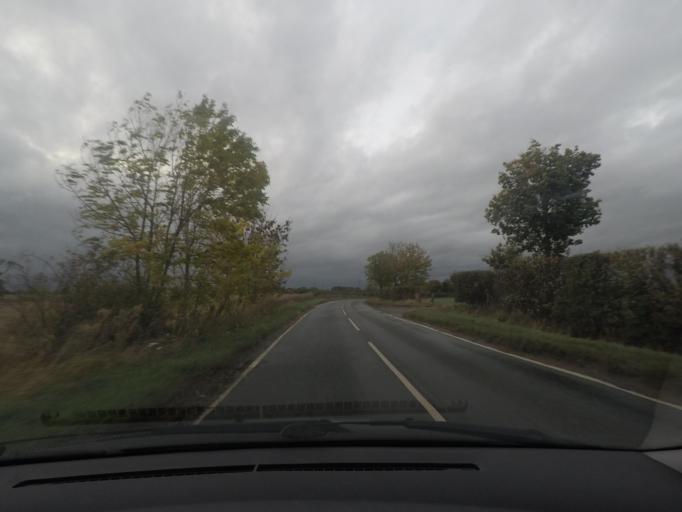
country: GB
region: England
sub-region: City of York
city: Wigginton
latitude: 54.0816
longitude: -1.1085
